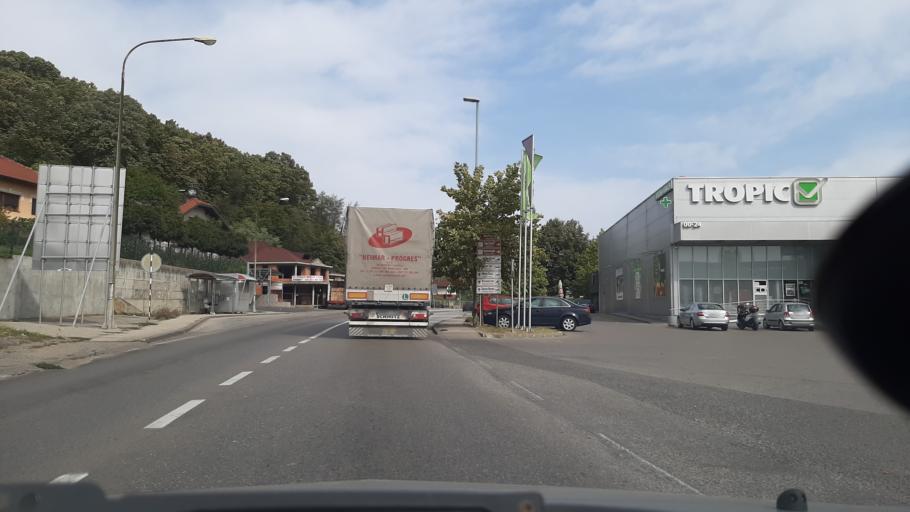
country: BA
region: Republika Srpska
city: Laktasi
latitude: 44.8793
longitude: 17.2838
